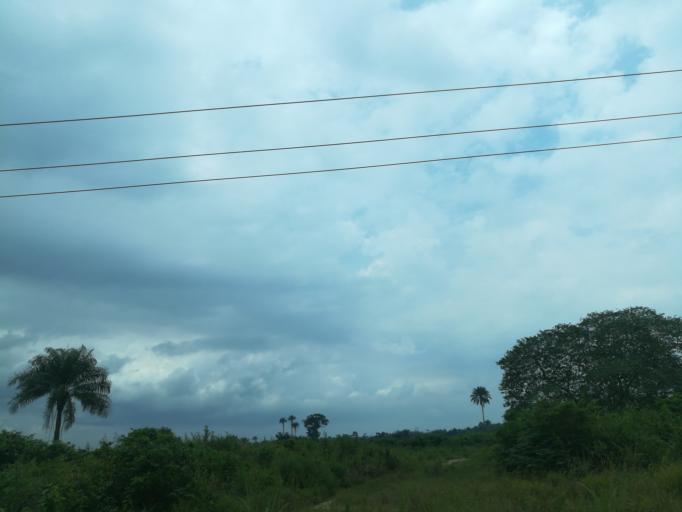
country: NG
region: Lagos
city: Ejirin
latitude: 6.6558
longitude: 3.8217
